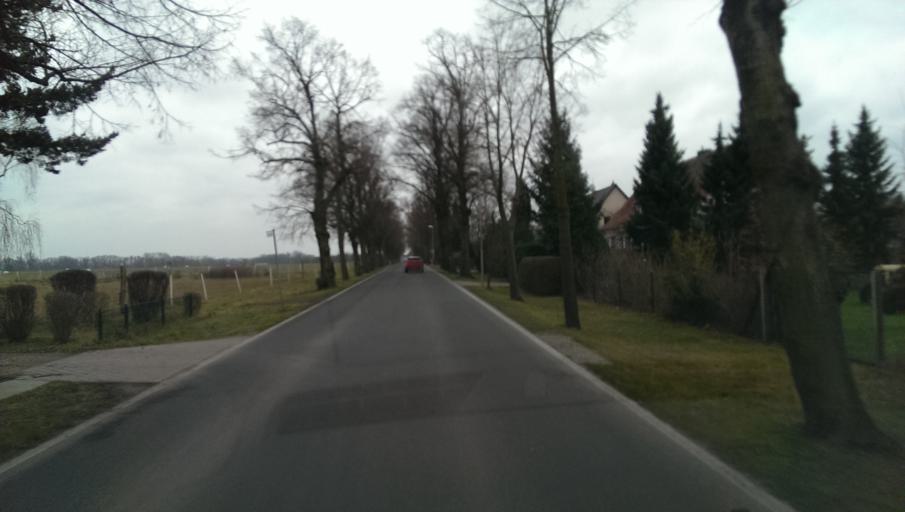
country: DE
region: Brandenburg
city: Grossbeeren
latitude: 52.3126
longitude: 13.3162
